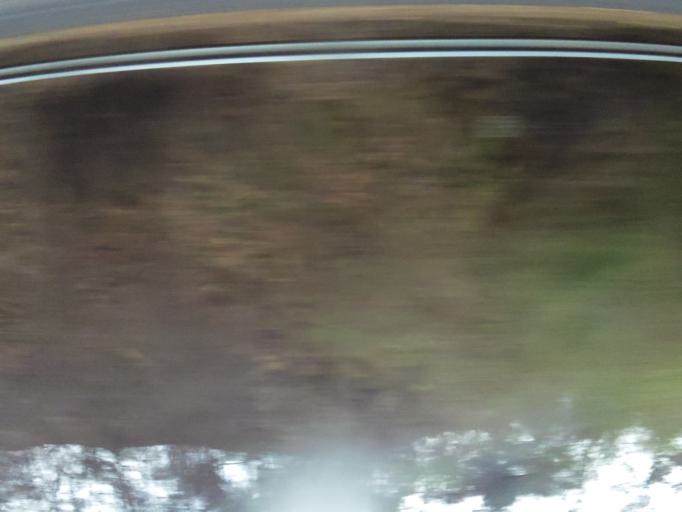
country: US
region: Alabama
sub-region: Blount County
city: Smoke Rise
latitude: 33.8976
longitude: -86.8584
